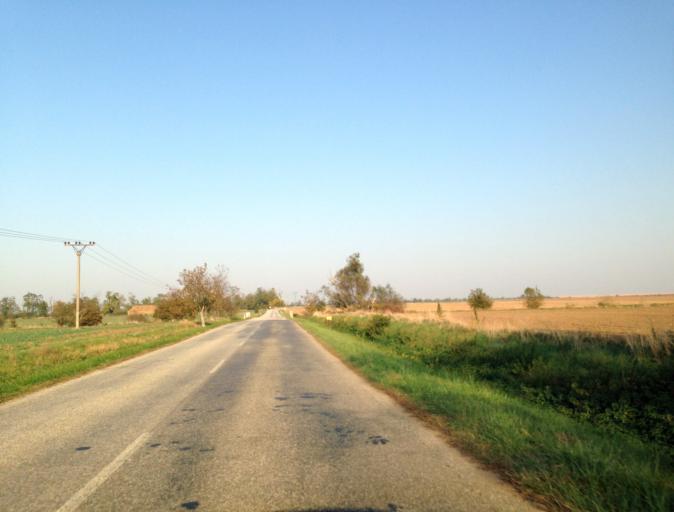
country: SK
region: Nitriansky
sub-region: Okres Komarno
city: Hurbanovo
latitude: 47.8920
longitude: 18.2236
